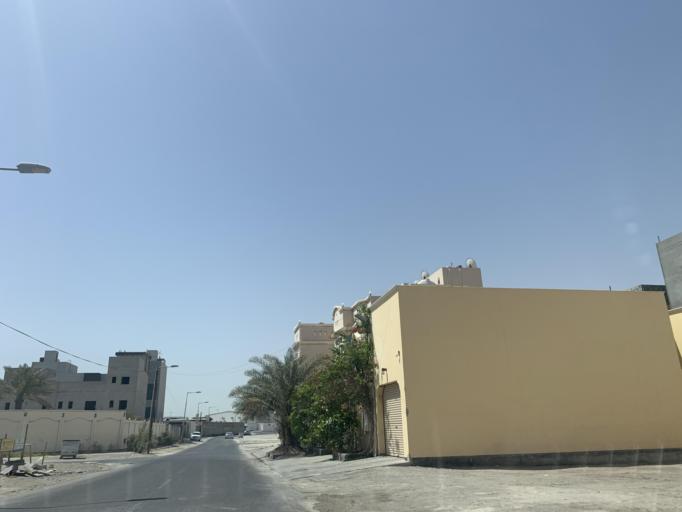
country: BH
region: Northern
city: Sitrah
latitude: 26.1578
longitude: 50.6119
